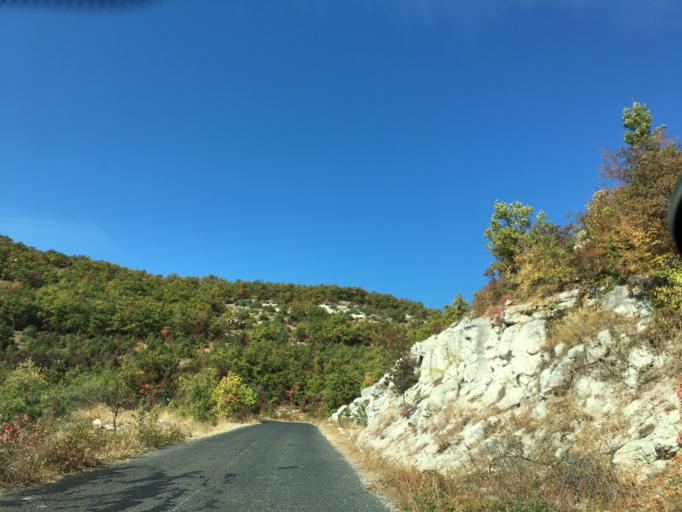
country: BG
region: Kurdzhali
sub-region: Obshtina Krumovgrad
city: Krumovgrad
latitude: 41.5501
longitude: 25.5535
